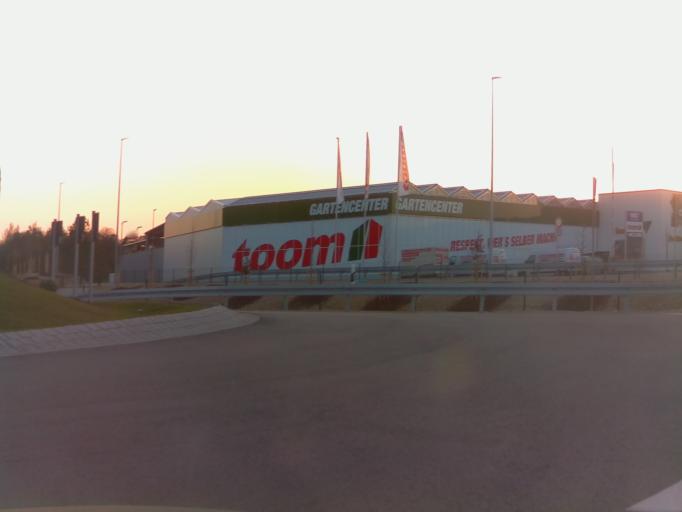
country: DE
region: Bavaria
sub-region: Upper Palatinate
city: Burglengenfeld
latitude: 49.1938
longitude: 12.0581
